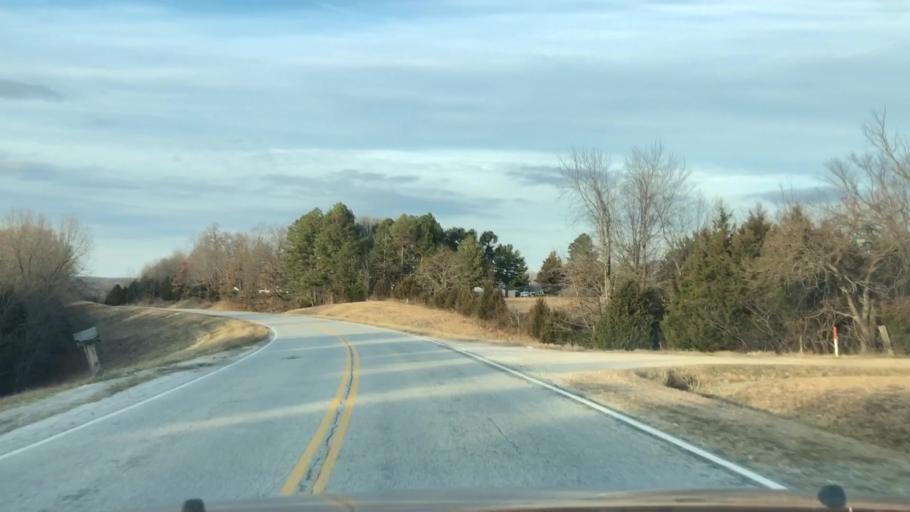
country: US
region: Missouri
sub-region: Webster County
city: Marshfield
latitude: 37.2350
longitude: -92.8790
